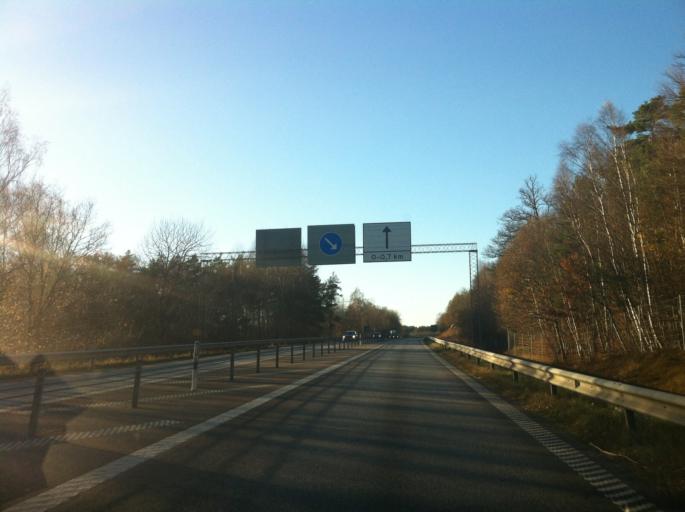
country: SE
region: Blekinge
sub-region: Karlshamns Kommun
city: Karlshamn
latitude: 56.1867
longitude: 14.8341
